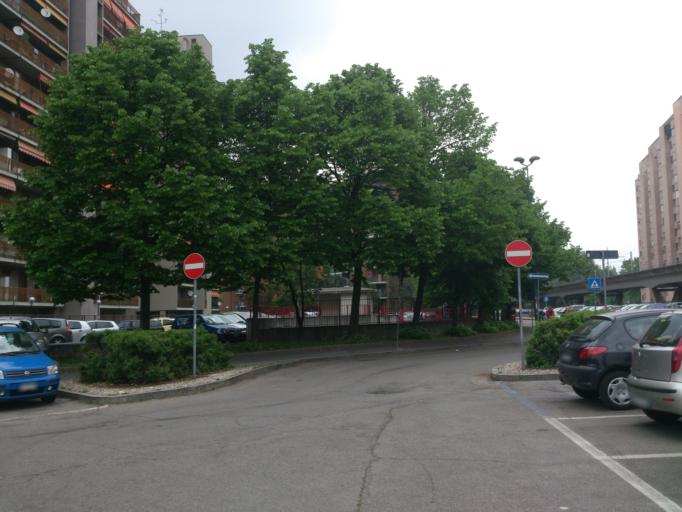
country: IT
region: Lombardy
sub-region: Citta metropolitana di Milano
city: Cologno Monzese
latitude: 45.5205
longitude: 9.2746
